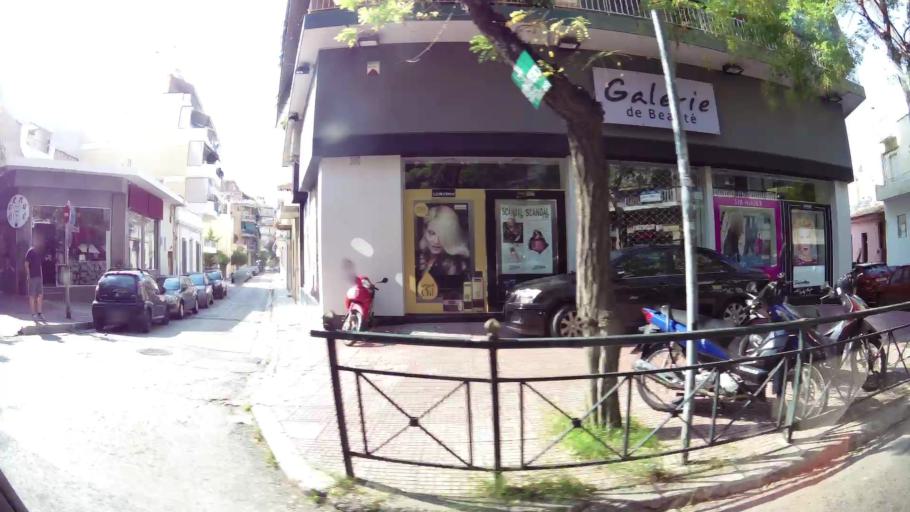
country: GR
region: Attica
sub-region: Nomarchia Athinas
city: Kipseli
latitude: 38.0040
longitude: 23.7182
